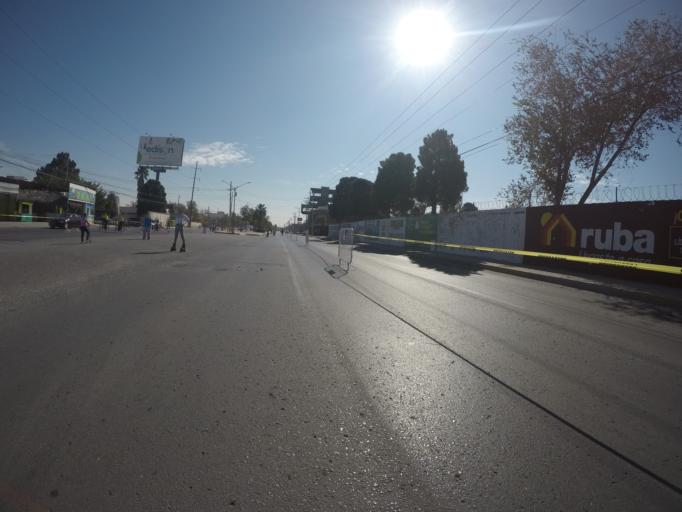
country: MX
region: Chihuahua
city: Ciudad Juarez
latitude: 31.7271
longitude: -106.4055
